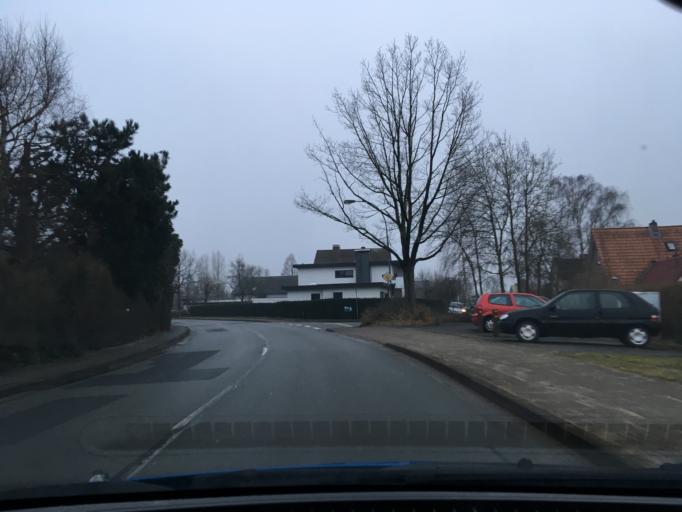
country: DE
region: Lower Saxony
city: Stelle
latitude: 53.4496
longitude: 10.0724
